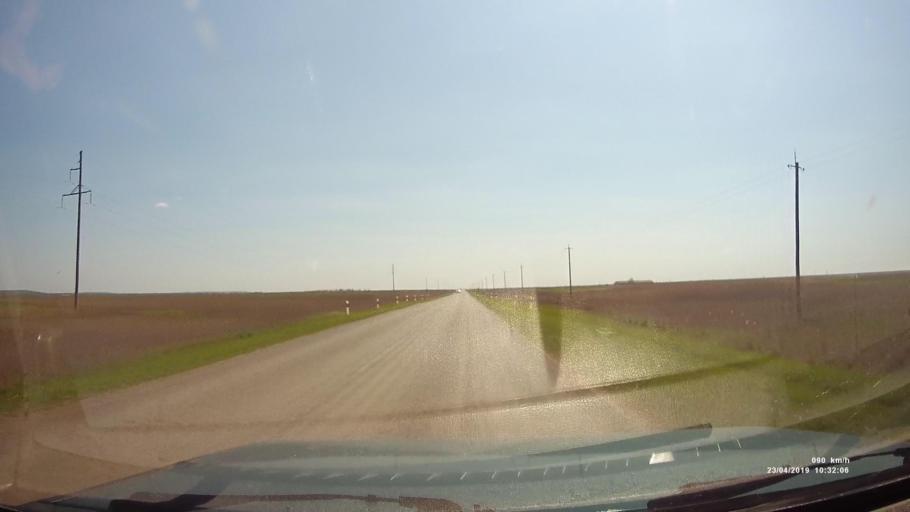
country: RU
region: Kalmykiya
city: Yashalta
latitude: 46.5823
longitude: 42.5720
